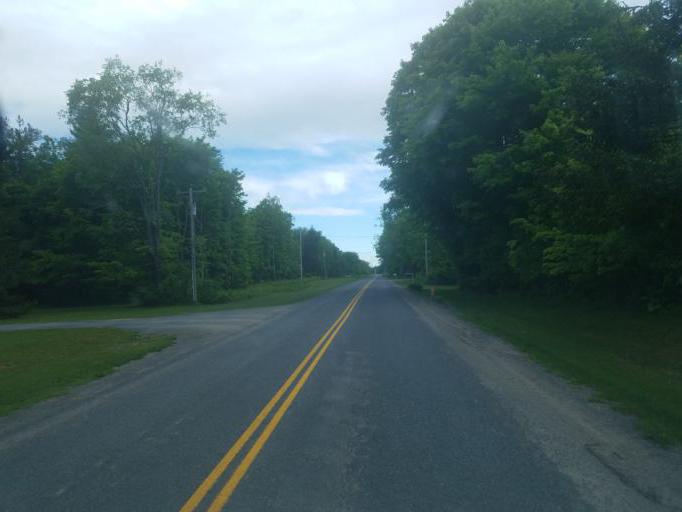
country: US
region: New York
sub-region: Herkimer County
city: Herkimer
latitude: 43.2528
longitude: -74.9794
